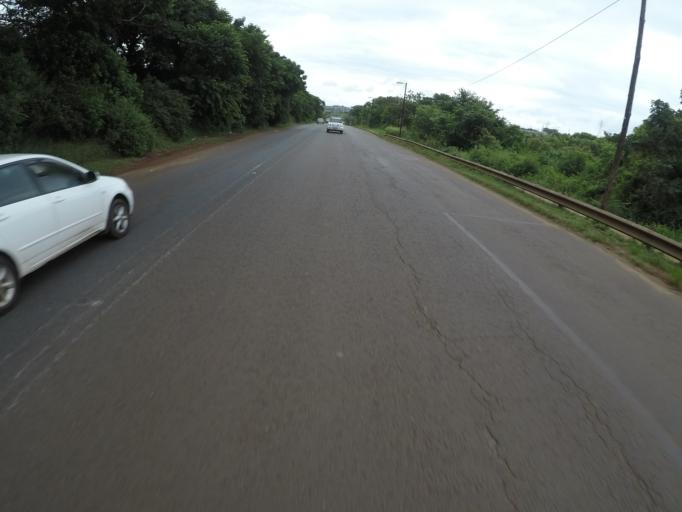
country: ZA
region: KwaZulu-Natal
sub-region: uThungulu District Municipality
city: Empangeni
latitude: -28.7762
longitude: 31.8861
